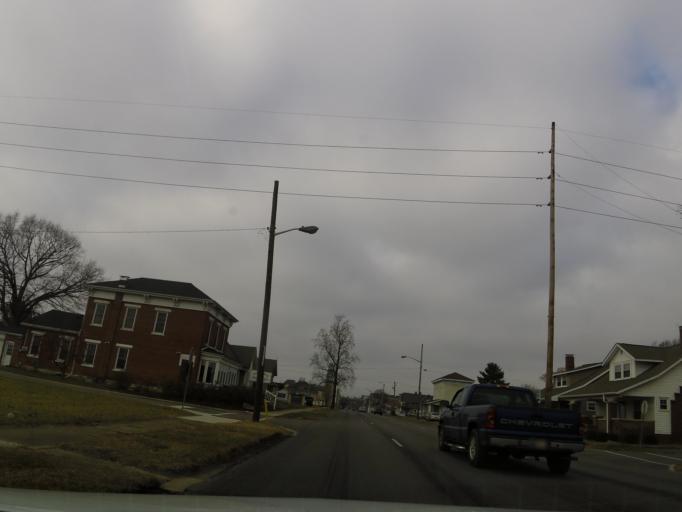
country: US
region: Indiana
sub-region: Bartholomew County
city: Columbus
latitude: 39.2016
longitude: -85.9154
